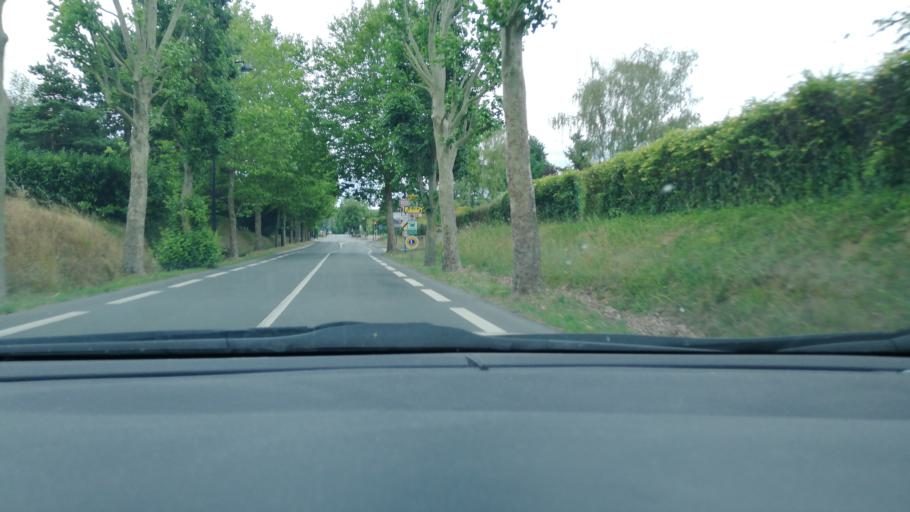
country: FR
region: Ile-de-France
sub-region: Departement du Val-d'Oise
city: Auvers-sur-Oise
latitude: 49.0775
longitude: 2.1601
